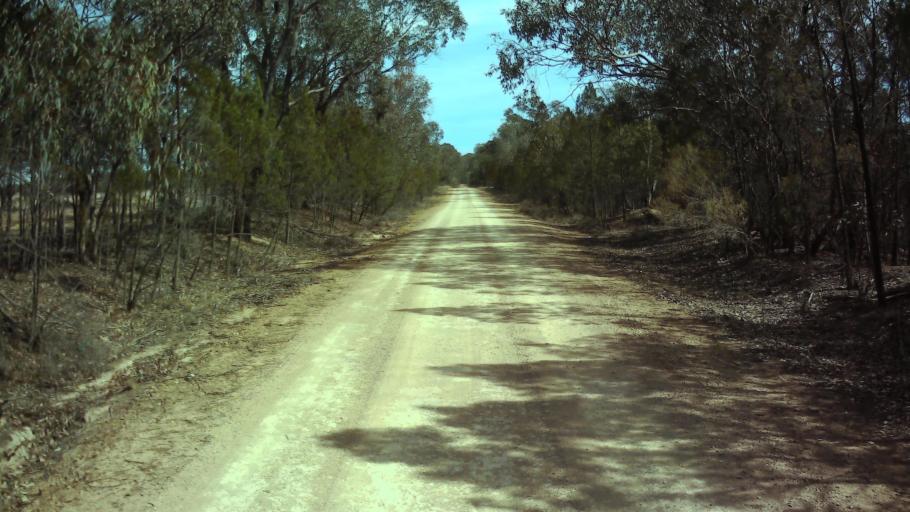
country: AU
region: New South Wales
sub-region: Weddin
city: Grenfell
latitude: -33.8744
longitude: 148.1485
